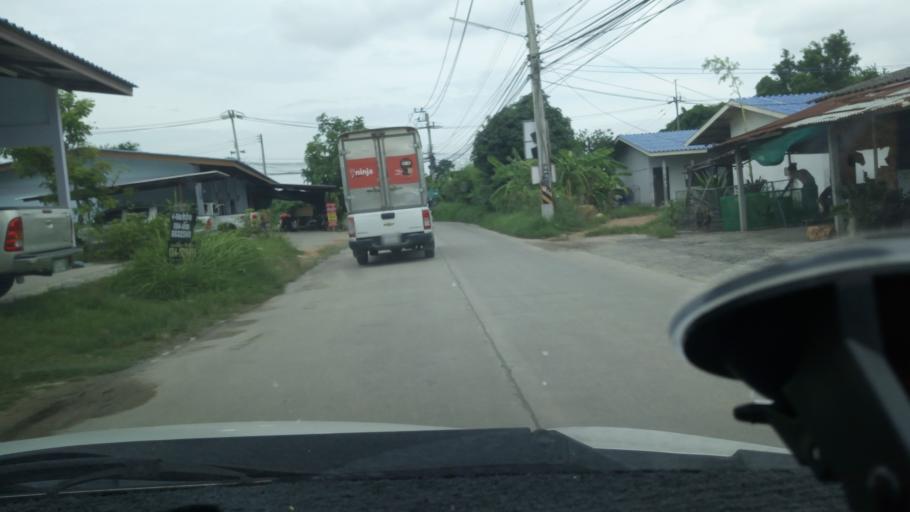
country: TH
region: Chon Buri
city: Chon Buri
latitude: 13.2816
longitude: 100.9633
